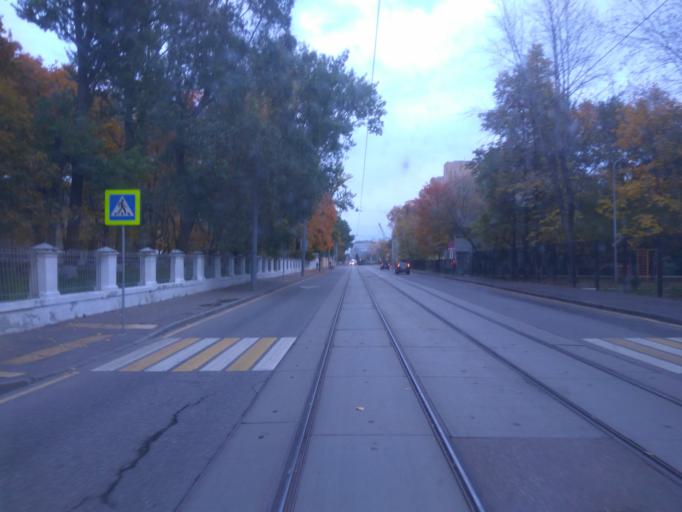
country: RU
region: Moscow
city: Mar'ina Roshcha
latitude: 55.7843
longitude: 37.6072
